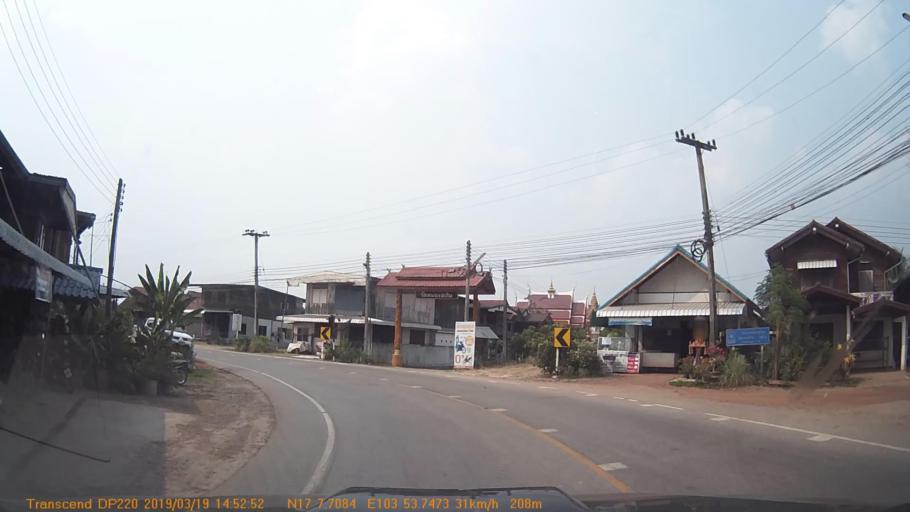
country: TH
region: Sakon Nakhon
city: Kut Bak
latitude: 17.1287
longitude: 103.8958
